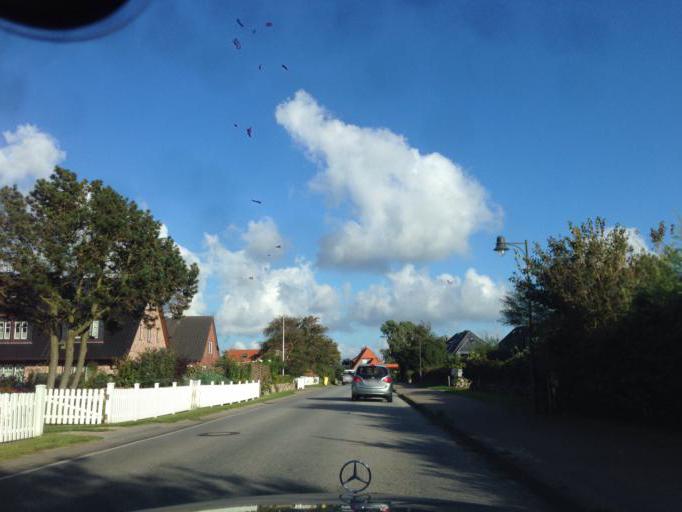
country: DE
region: Schleswig-Holstein
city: Sylt-Ost
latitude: 54.8708
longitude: 8.4250
